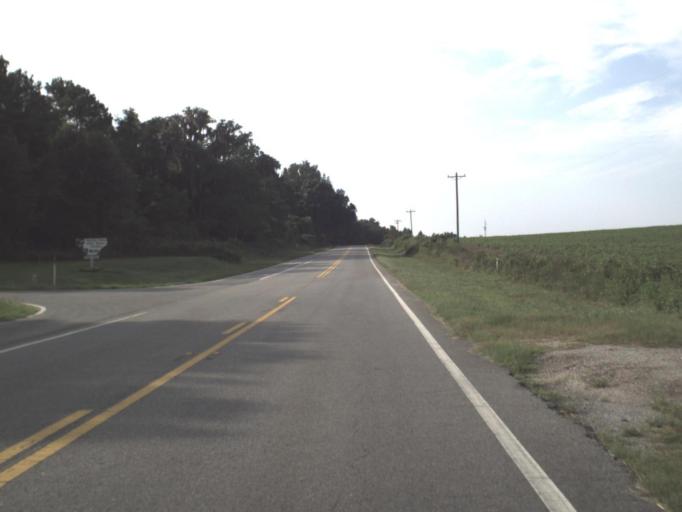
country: US
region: Florida
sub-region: Madison County
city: Madison
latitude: 30.4528
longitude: -83.6289
